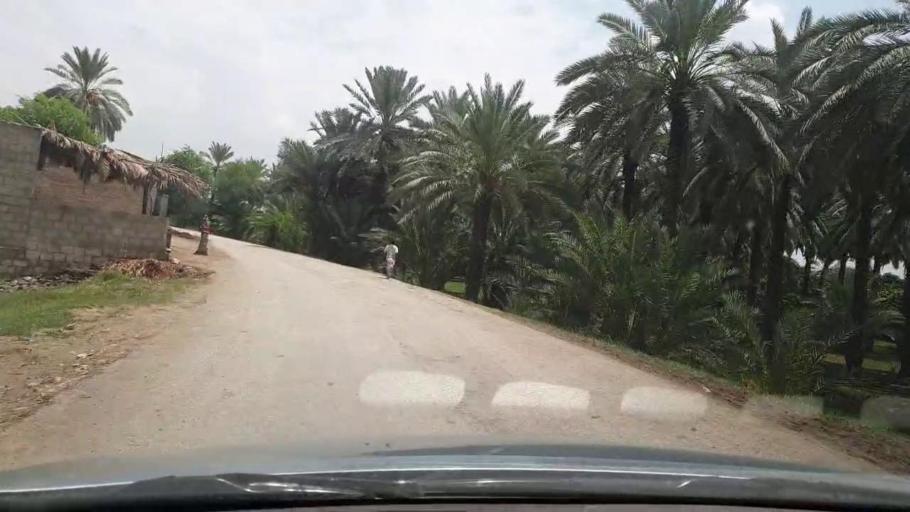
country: PK
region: Sindh
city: Khairpur
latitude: 27.4327
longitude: 68.7677
